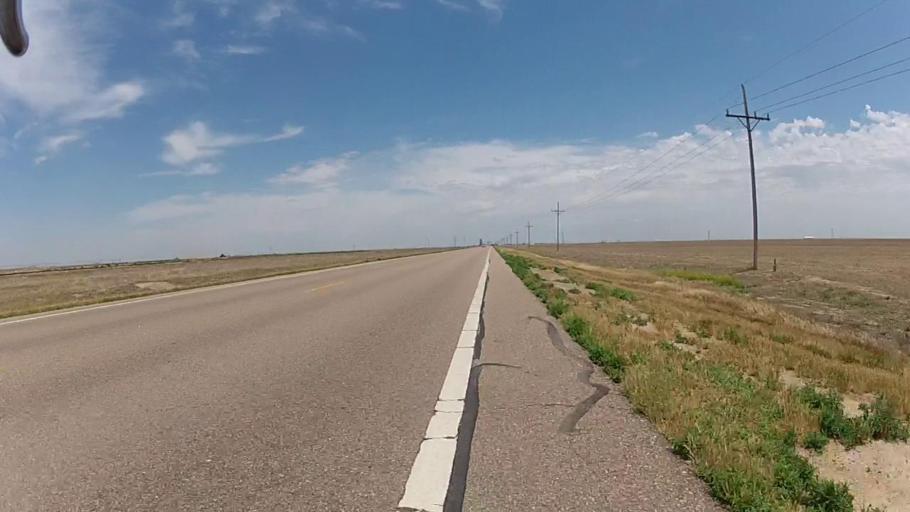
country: US
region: Kansas
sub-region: Haskell County
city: Sublette
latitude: 37.4662
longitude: -100.9055
